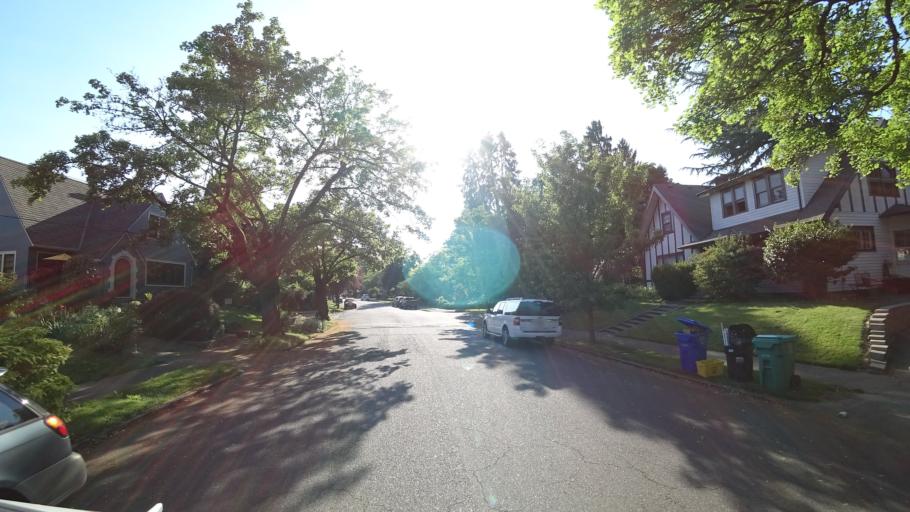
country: US
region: Oregon
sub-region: Multnomah County
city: Portland
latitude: 45.5494
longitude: -122.6417
